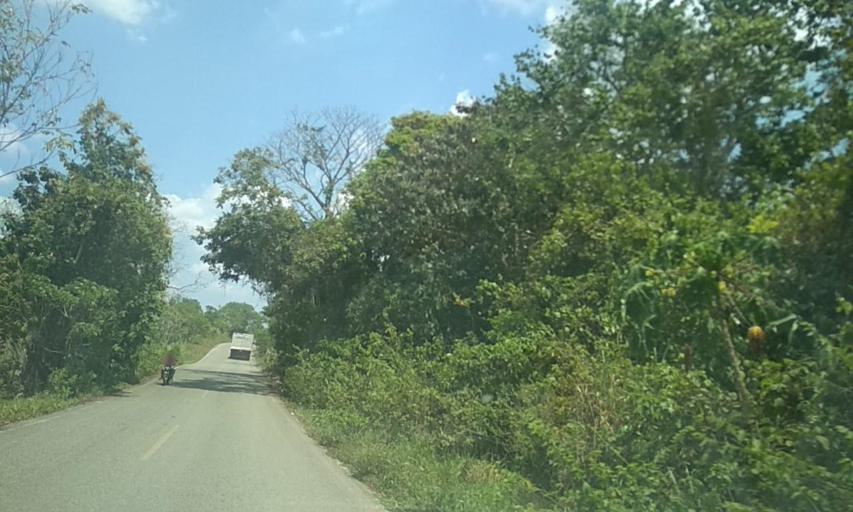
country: MX
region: Tabasco
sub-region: Huimanguillo
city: Francisco Rueda
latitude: 17.7734
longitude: -93.8088
